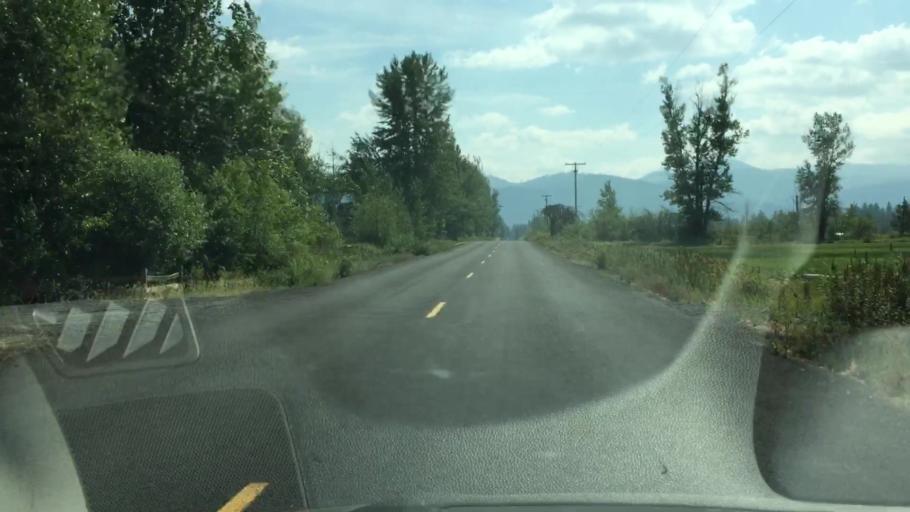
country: US
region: Washington
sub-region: Klickitat County
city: White Salmon
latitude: 46.0121
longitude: -121.5287
